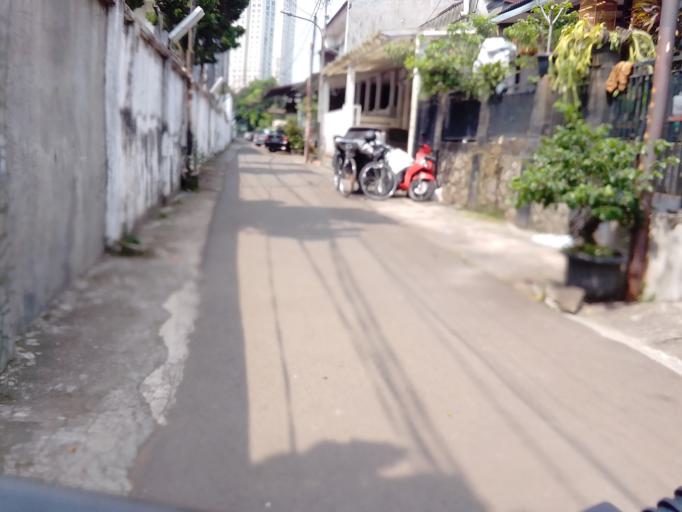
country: ID
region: Jakarta Raya
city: Jakarta
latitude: -6.2114
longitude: 106.8098
